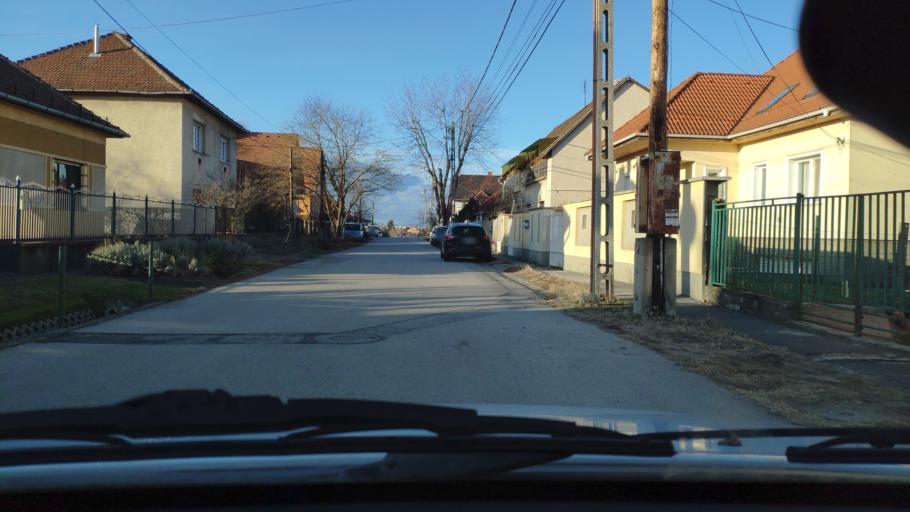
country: HU
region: Budapest
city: Budapest XXIII. keruelet
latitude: 47.3968
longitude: 19.0950
